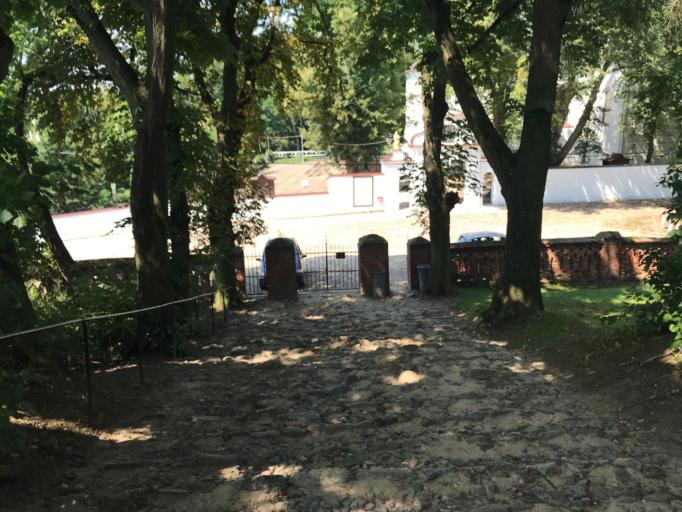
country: PL
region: Kujawsko-Pomorskie
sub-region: Powiat golubsko-dobrzynski
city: Zbojno
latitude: 53.0008
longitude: 19.2140
